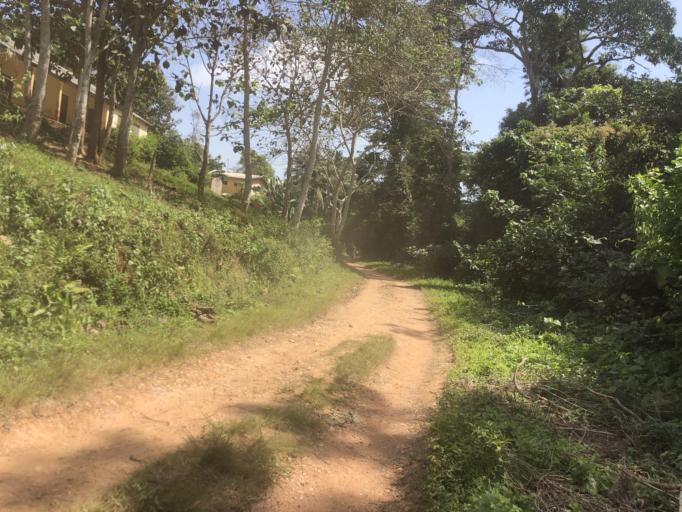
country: TG
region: Plateaux
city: Kpalime
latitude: 6.8453
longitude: 0.4375
